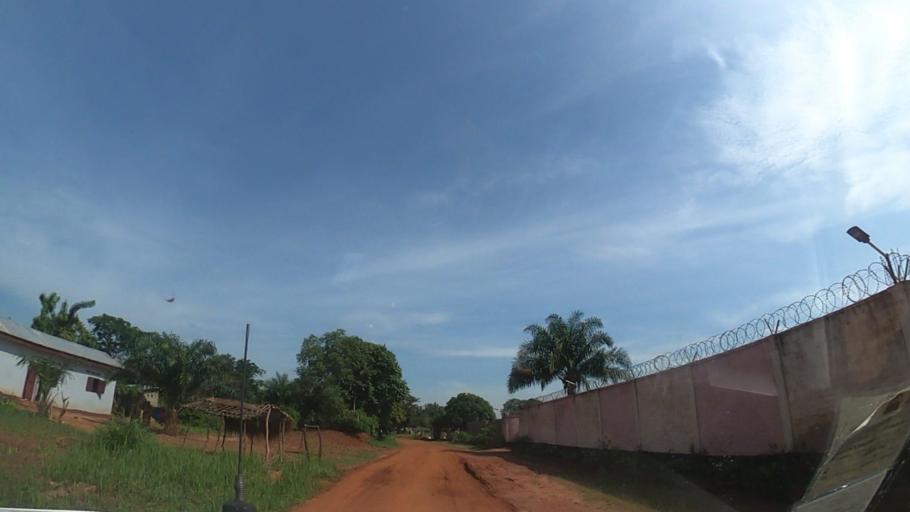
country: CF
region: Ombella-Mpoko
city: Bimbo
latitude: 4.3157
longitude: 18.4690
